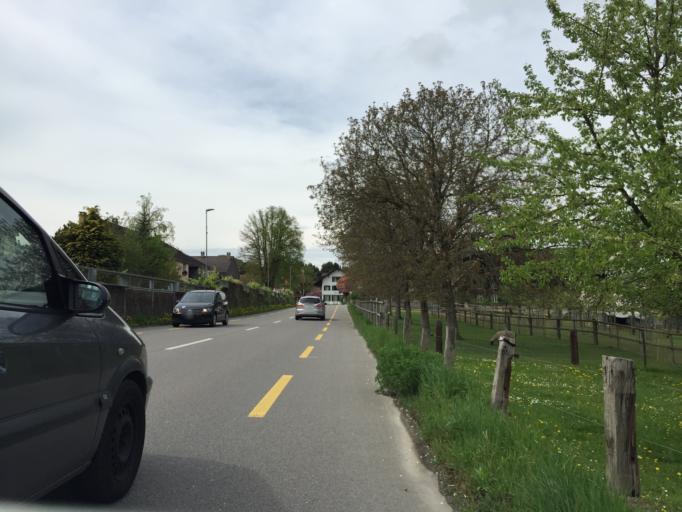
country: CH
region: Bern
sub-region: Bern-Mittelland District
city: Rubigen
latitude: 46.9136
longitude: 7.5256
